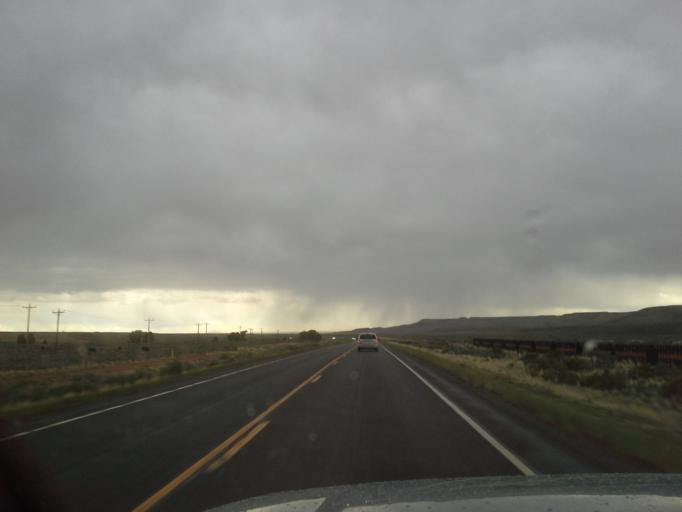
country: US
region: Wyoming
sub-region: Park County
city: Powell
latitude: 45.0519
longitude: -108.6548
